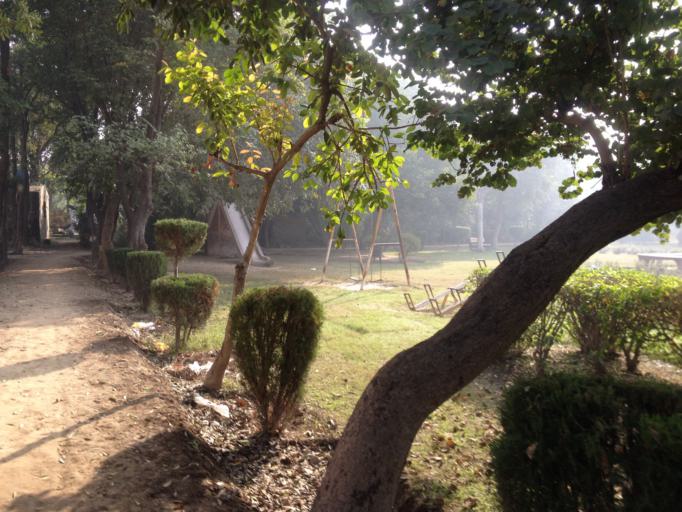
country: PK
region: Punjab
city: Lahore
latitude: 31.4665
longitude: 74.3004
